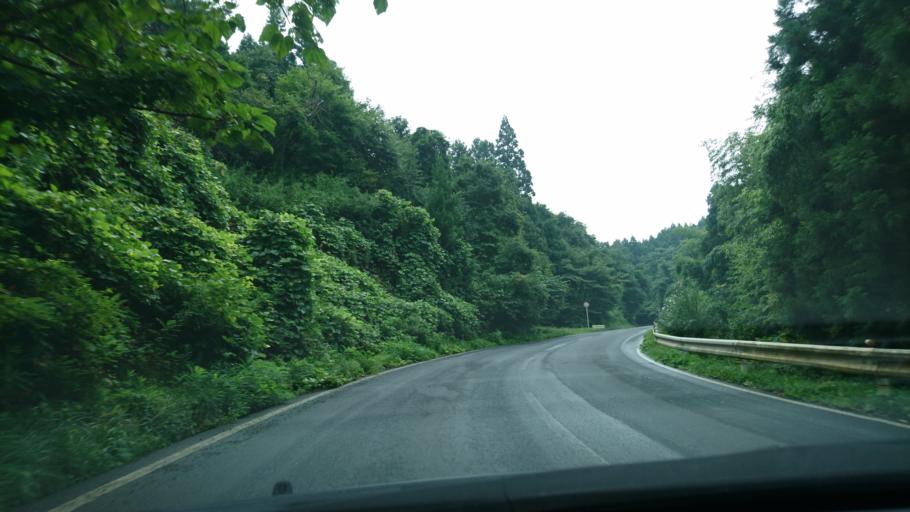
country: JP
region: Iwate
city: Ichinoseki
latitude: 38.9388
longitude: 141.1823
